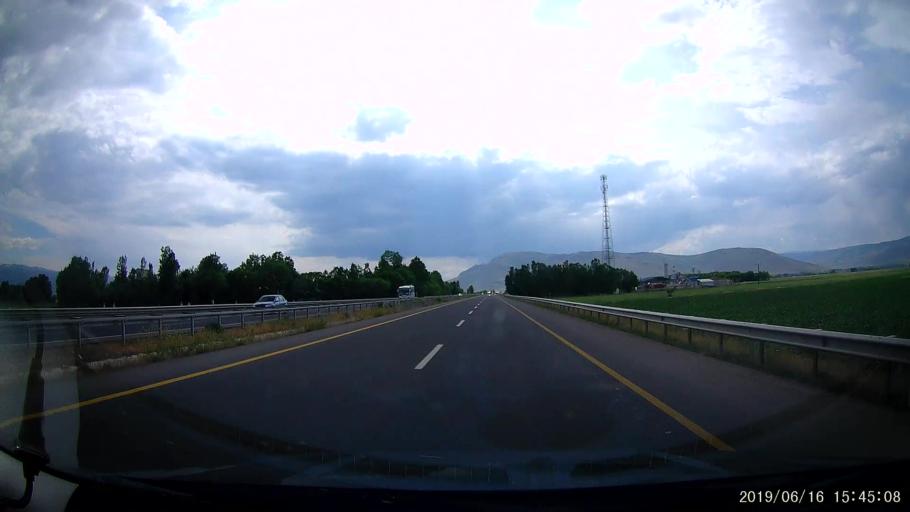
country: TR
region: Erzurum
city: Koprukoy
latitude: 39.9879
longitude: 41.7735
